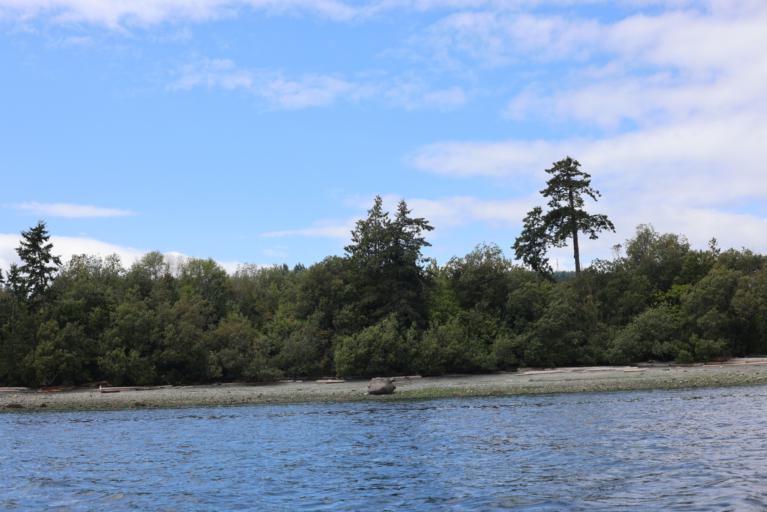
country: CA
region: British Columbia
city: North Saanich
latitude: 48.6222
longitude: -123.4040
